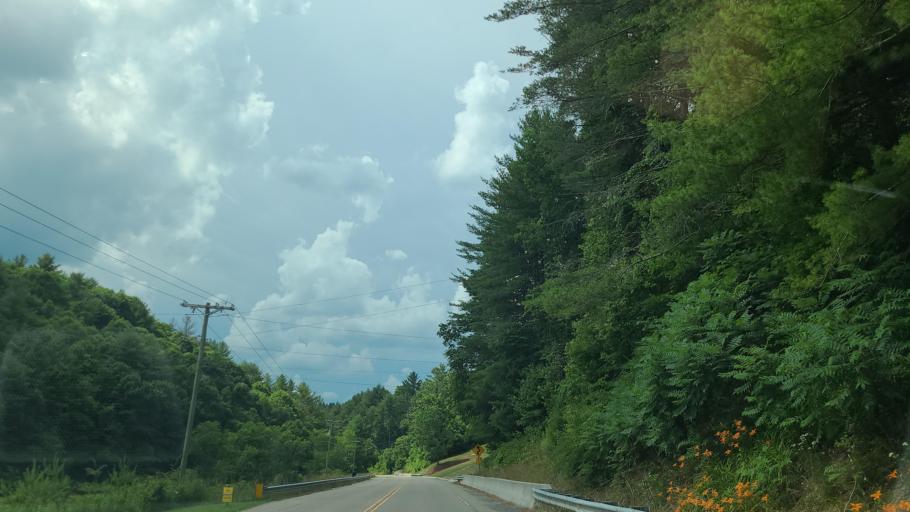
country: US
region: North Carolina
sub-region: Ashe County
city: Jefferson
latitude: 36.3673
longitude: -81.3912
